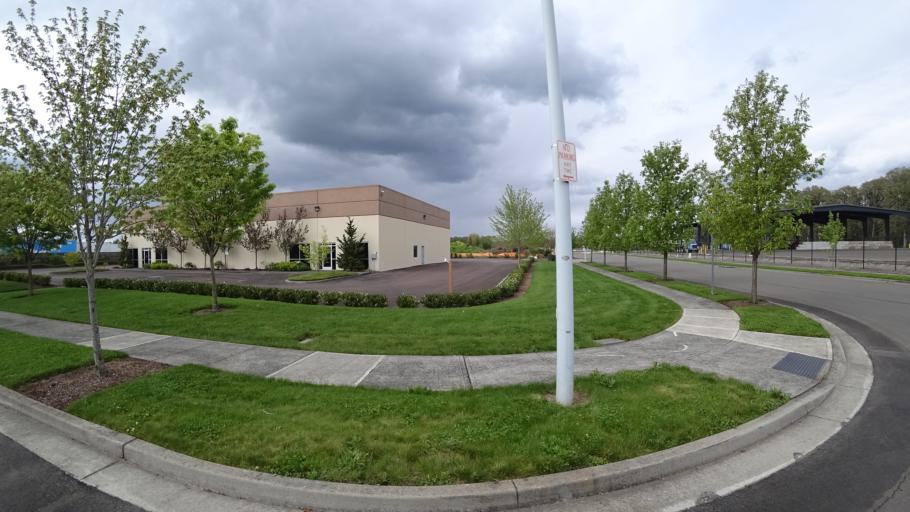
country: US
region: Oregon
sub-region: Washington County
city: Hillsboro
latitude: 45.5477
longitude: -122.9459
